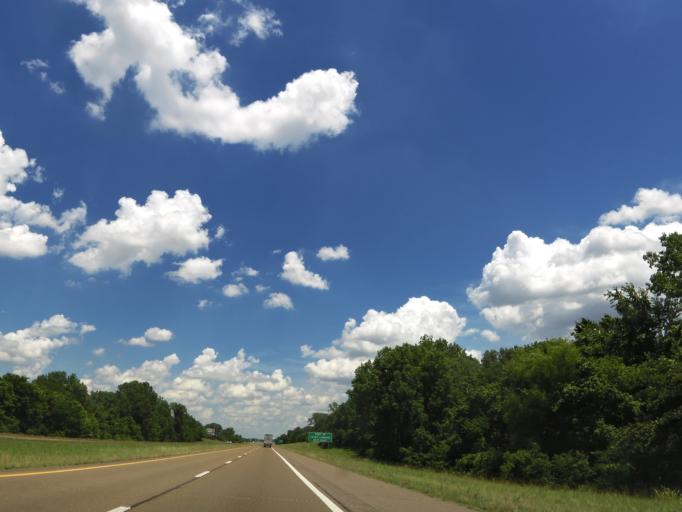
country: US
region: Tennessee
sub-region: Dyer County
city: Dyersburg
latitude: 36.0689
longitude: -89.4170
